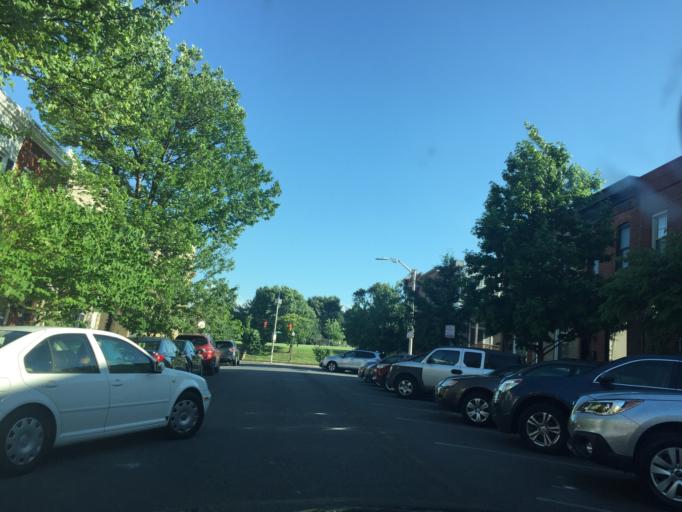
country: US
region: Maryland
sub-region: City of Baltimore
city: Baltimore
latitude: 39.2927
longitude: -76.5819
